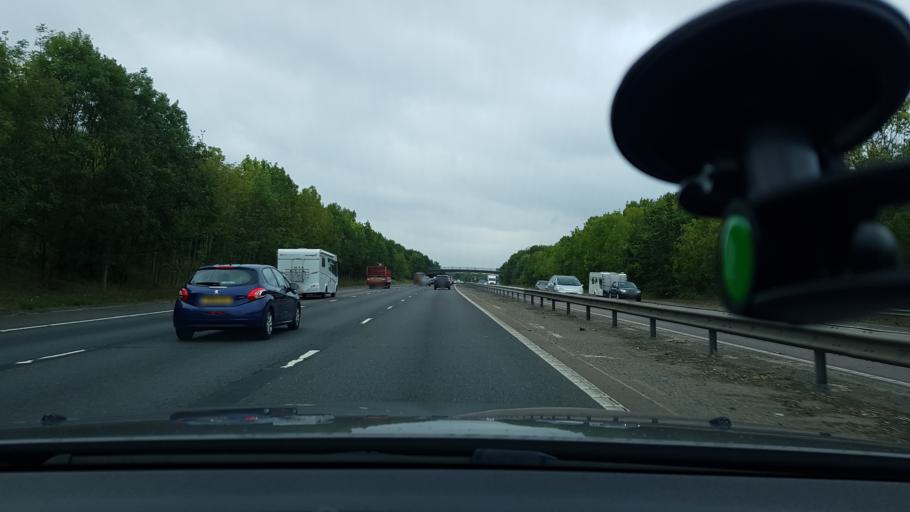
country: GB
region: England
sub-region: Hertfordshire
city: Sawbridgeworth
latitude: 51.7805
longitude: 0.1667
